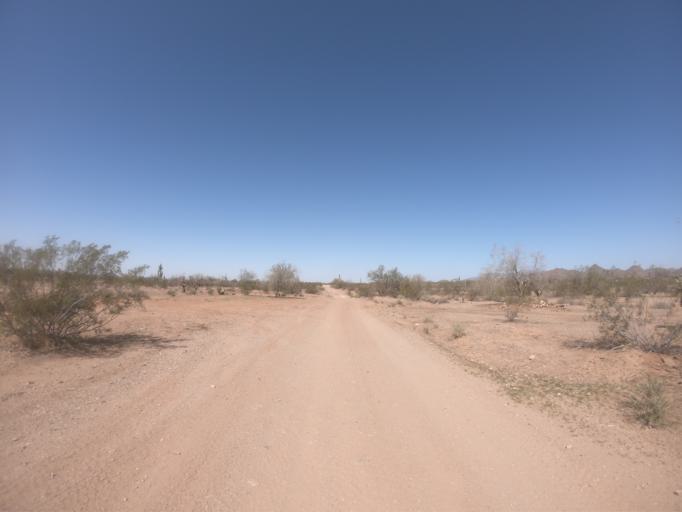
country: US
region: Arizona
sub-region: Pinal County
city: Gold Camp
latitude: 33.2423
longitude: -111.3185
